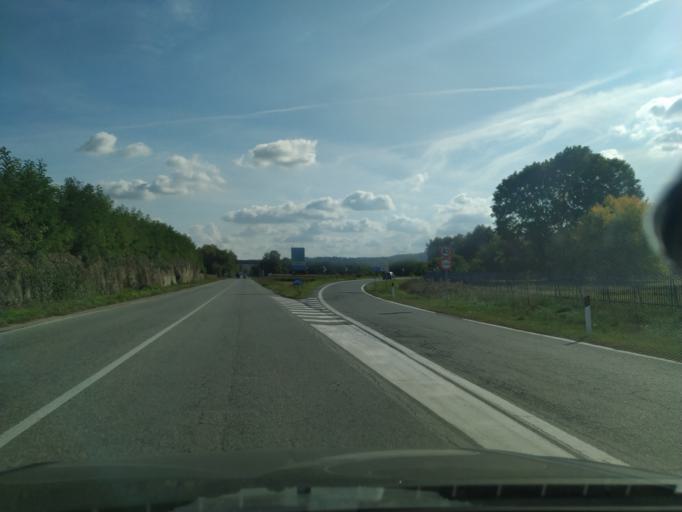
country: IT
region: Piedmont
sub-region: Provincia di Biella
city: Vergnasco
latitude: 45.4824
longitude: 8.0910
